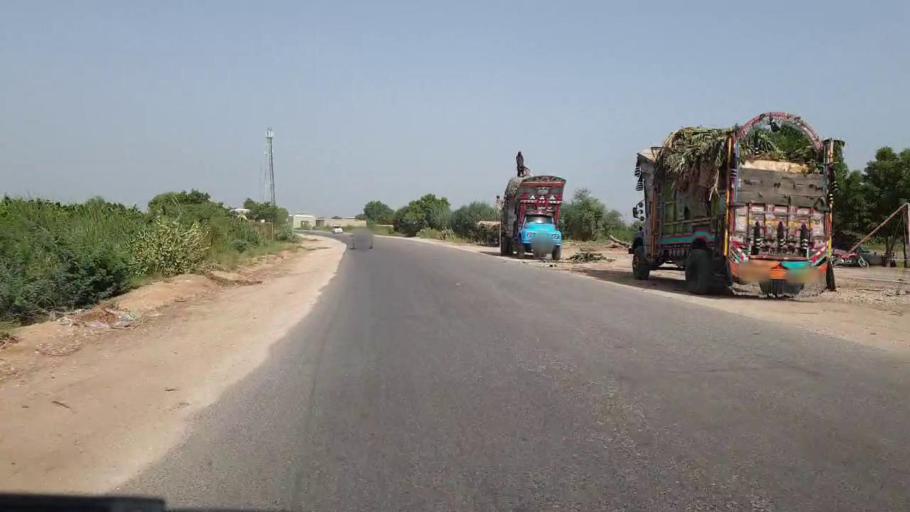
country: PK
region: Sindh
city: Sakrand
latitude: 26.2460
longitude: 68.2183
